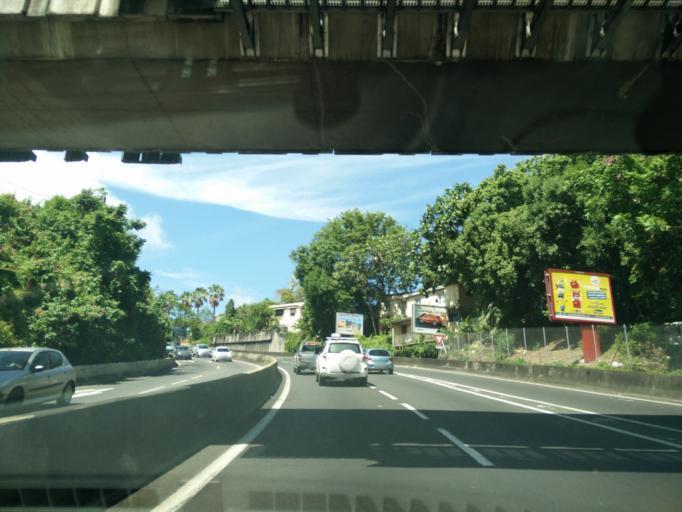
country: MQ
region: Martinique
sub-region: Martinique
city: Fort-de-France
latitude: 14.6095
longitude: -61.0658
